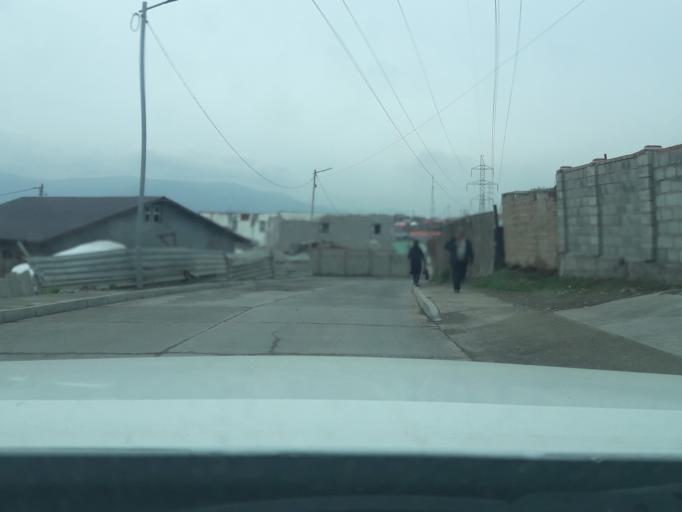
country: MN
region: Ulaanbaatar
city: Ulaanbaatar
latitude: 47.9479
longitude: 106.9041
